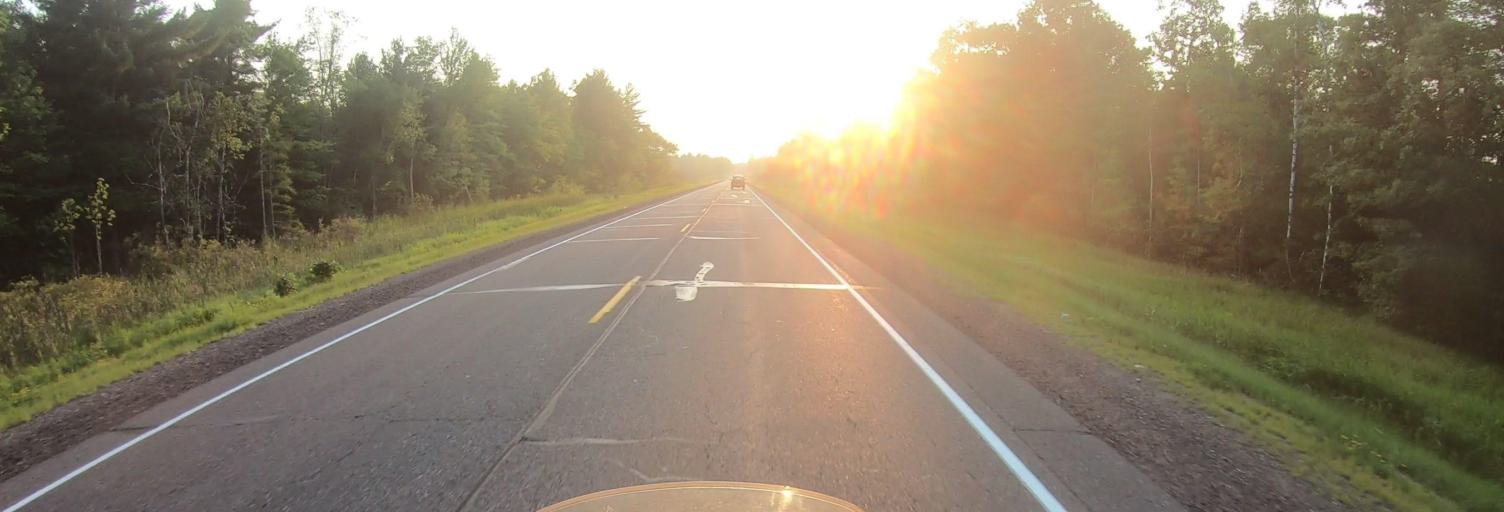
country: US
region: Wisconsin
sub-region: Burnett County
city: Siren
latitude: 45.7705
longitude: -92.4948
